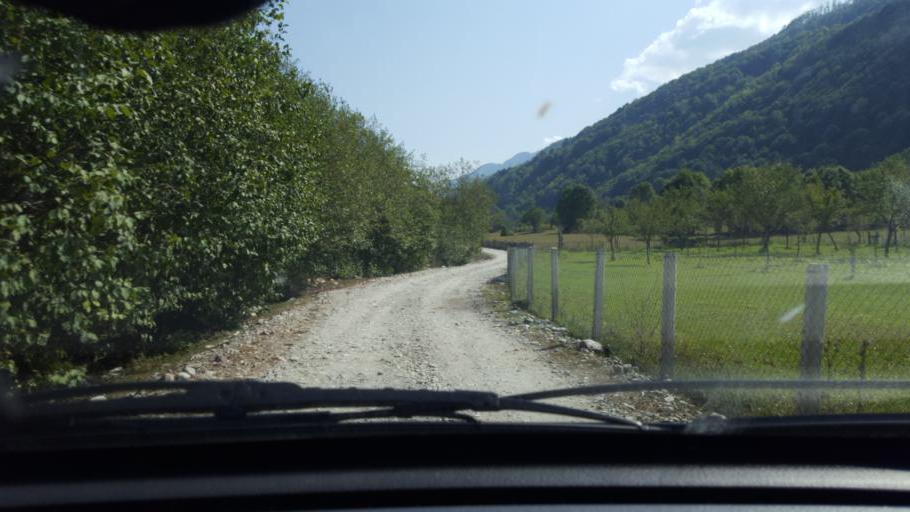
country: ME
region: Andrijevica
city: Andrijevica
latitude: 42.5909
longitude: 19.6878
